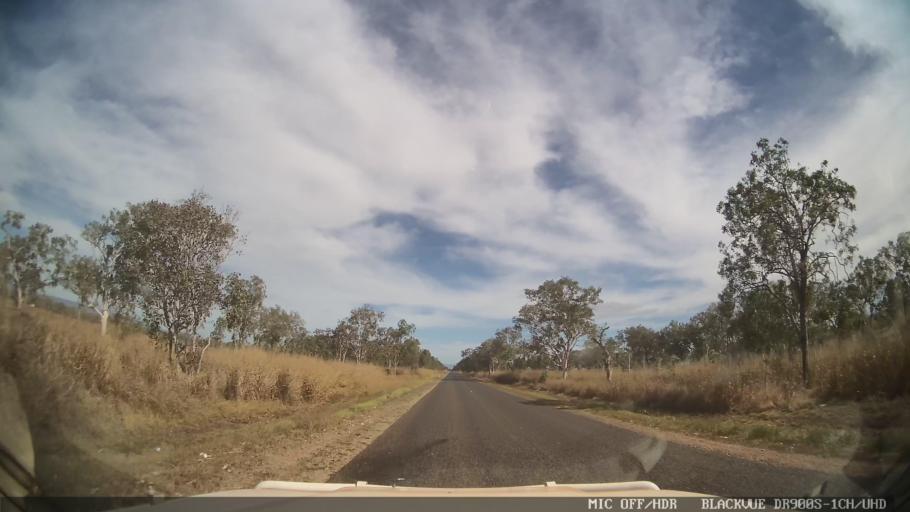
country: AU
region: Queensland
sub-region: Tablelands
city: Mareeba
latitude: -16.9397
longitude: 145.4168
